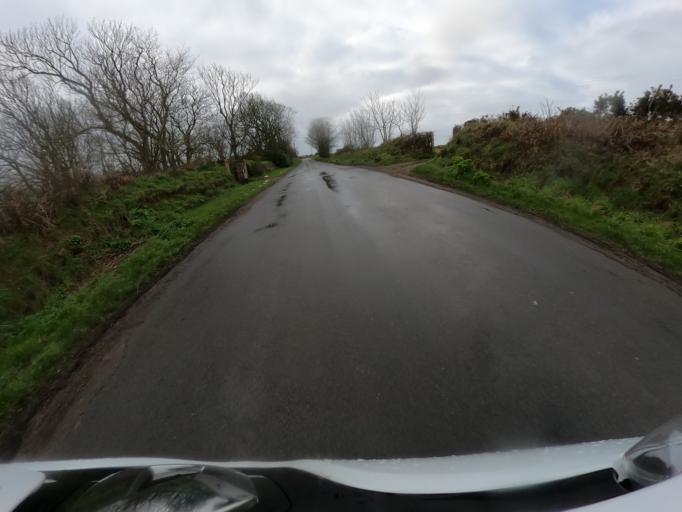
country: IM
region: Ramsey
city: Ramsey
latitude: 54.3636
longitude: -4.5102
